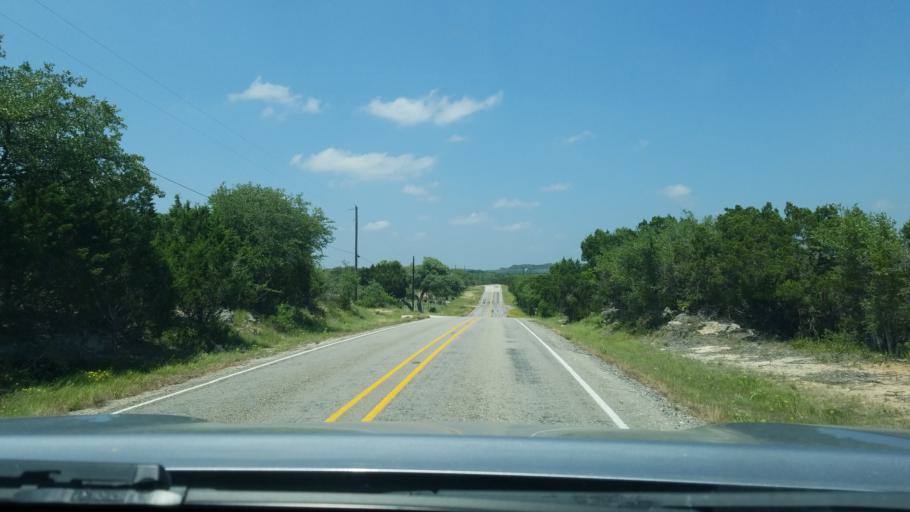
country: US
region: Texas
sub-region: Hays County
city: Woodcreek
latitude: 30.0866
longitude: -98.2283
